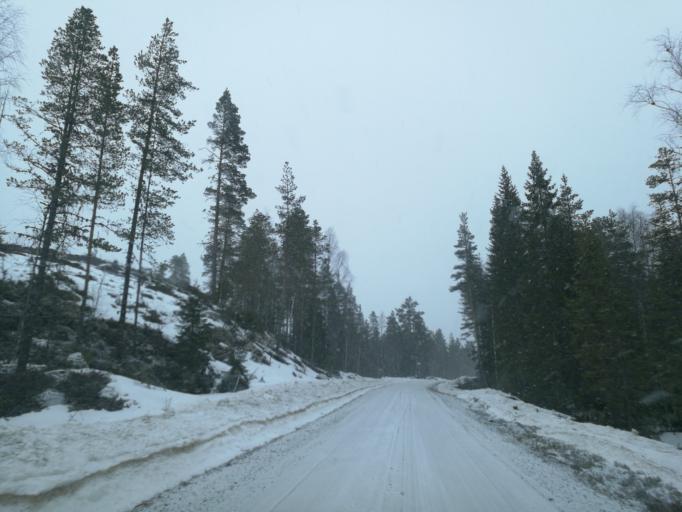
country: SE
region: Vaermland
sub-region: Torsby Kommun
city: Torsby
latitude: 60.6443
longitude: 12.7984
